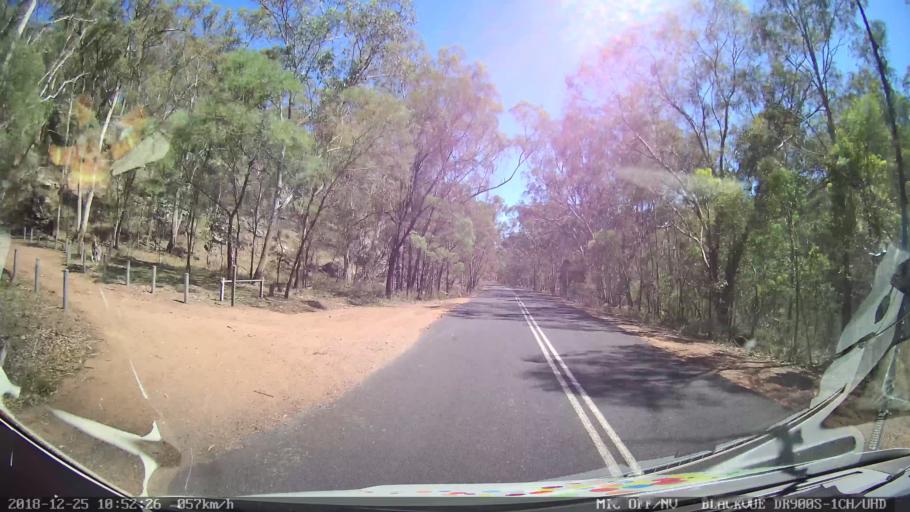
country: AU
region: New South Wales
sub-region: Upper Hunter Shire
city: Merriwa
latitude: -32.4288
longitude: 150.2734
